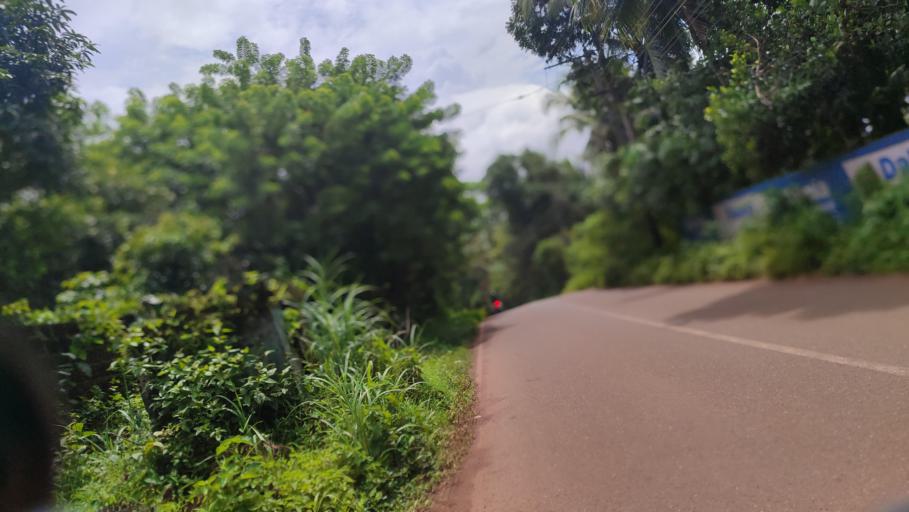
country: IN
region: Kerala
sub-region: Kasaragod District
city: Kannangad
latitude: 12.3938
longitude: 75.0532
